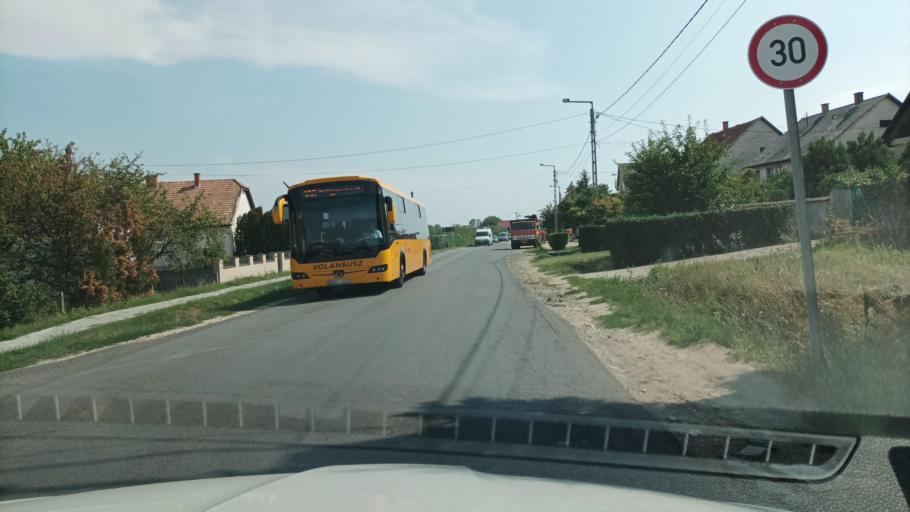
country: HU
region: Pest
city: Galgaheviz
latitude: 47.6180
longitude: 19.5735
